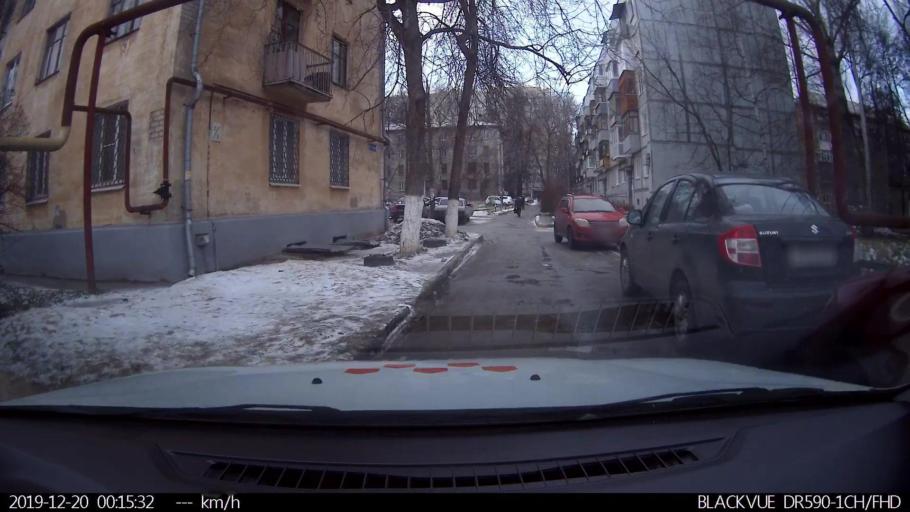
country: RU
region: Jaroslavl
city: Porech'ye-Rybnoye
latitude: 56.9861
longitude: 39.3906
